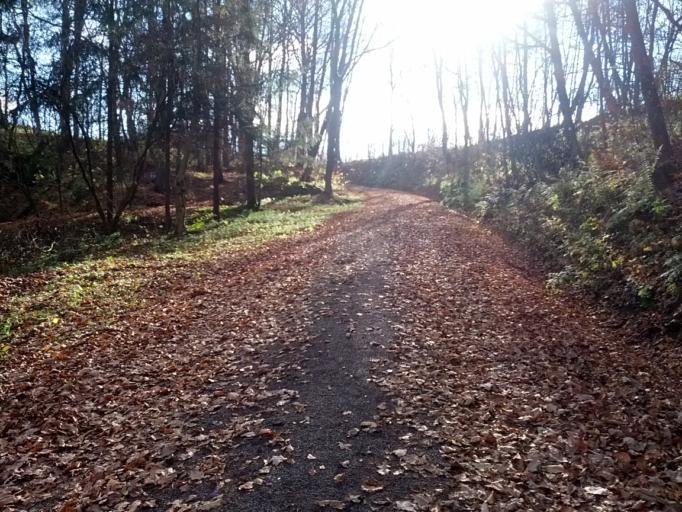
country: DE
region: Thuringia
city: Krauthausen
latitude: 51.0015
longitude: 10.2250
